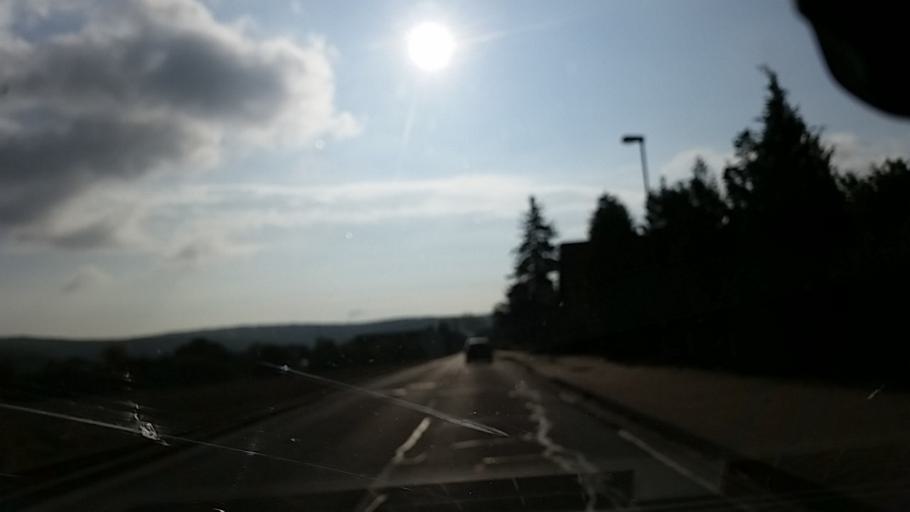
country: DE
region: Thuringia
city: Kleinfurra
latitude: 51.4134
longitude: 10.7600
